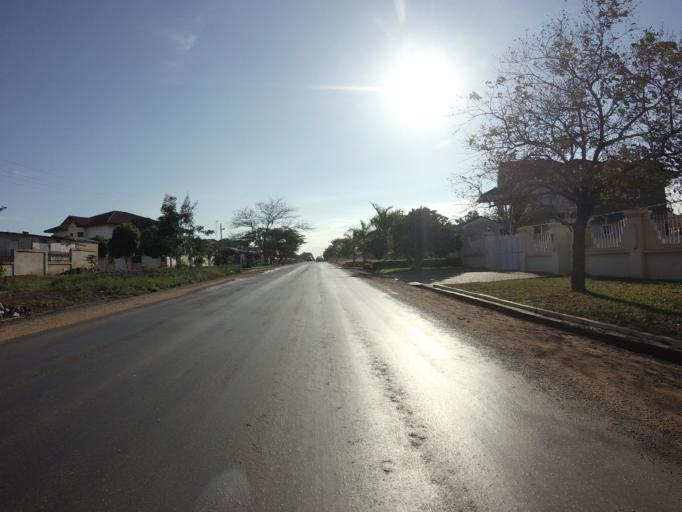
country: GH
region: Greater Accra
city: Nungua
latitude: 5.6519
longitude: -0.0677
